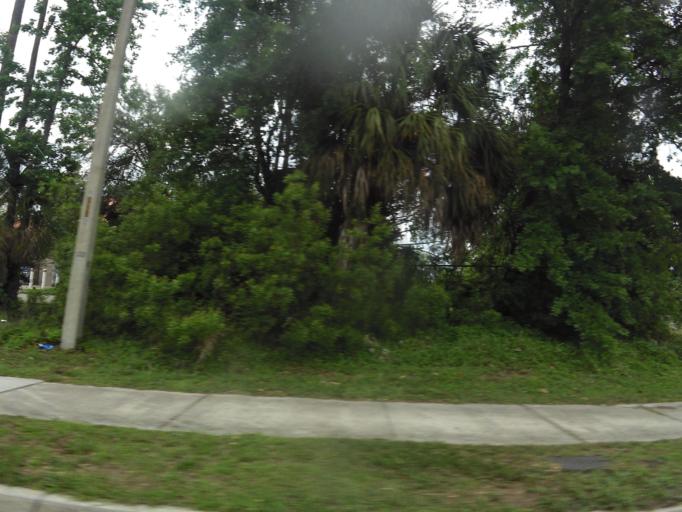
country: US
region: Florida
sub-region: Duval County
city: Jacksonville
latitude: 30.2997
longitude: -81.7509
